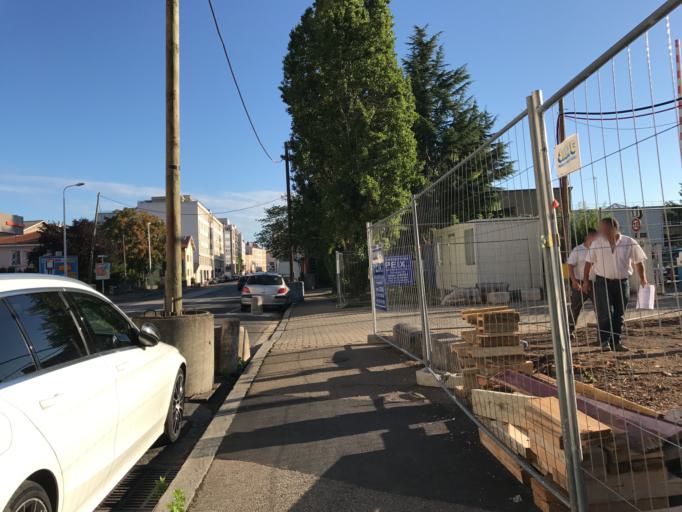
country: FR
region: Rhone-Alpes
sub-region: Departement du Rhone
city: Lyon
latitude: 45.7345
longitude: 4.8396
